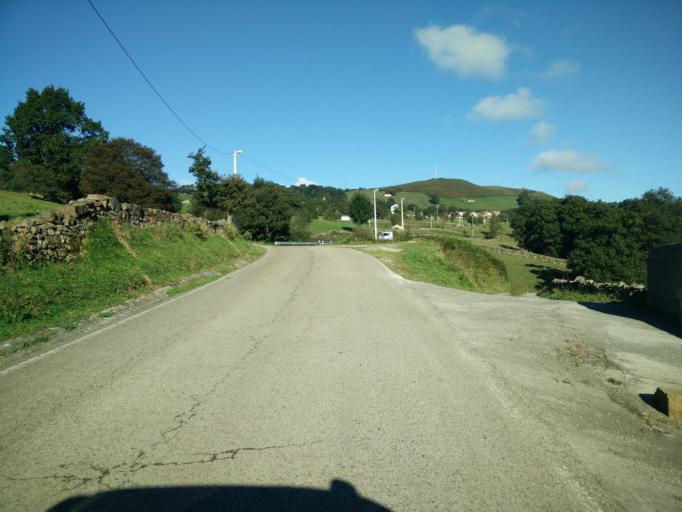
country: ES
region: Cantabria
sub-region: Provincia de Cantabria
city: San Pedro del Romeral
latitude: 43.1113
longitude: -3.8105
